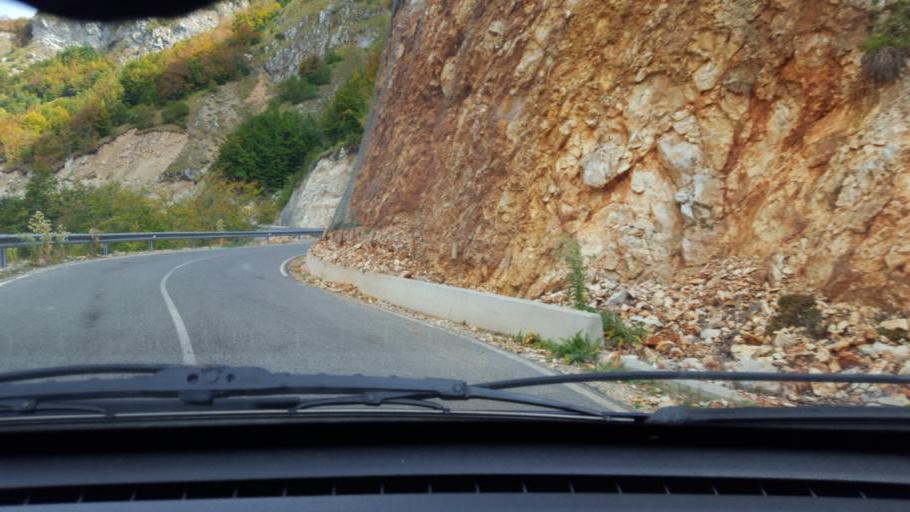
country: ME
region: Andrijevica
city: Andrijevica
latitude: 42.5348
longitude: 19.6771
